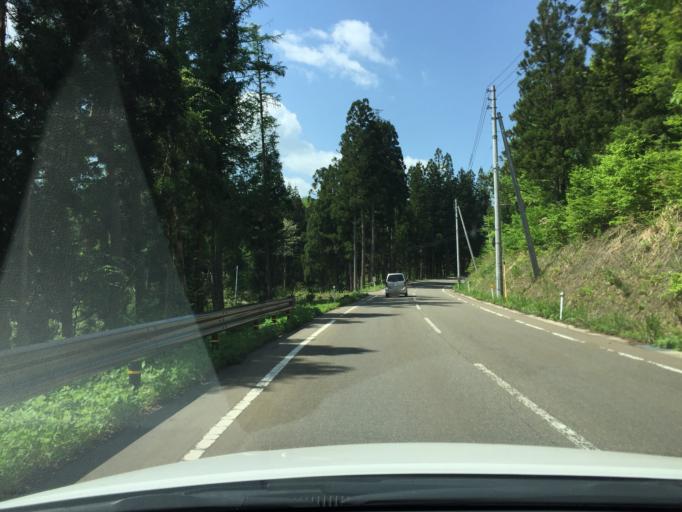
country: JP
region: Niigata
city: Tochio-honcho
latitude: 37.4698
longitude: 139.0356
